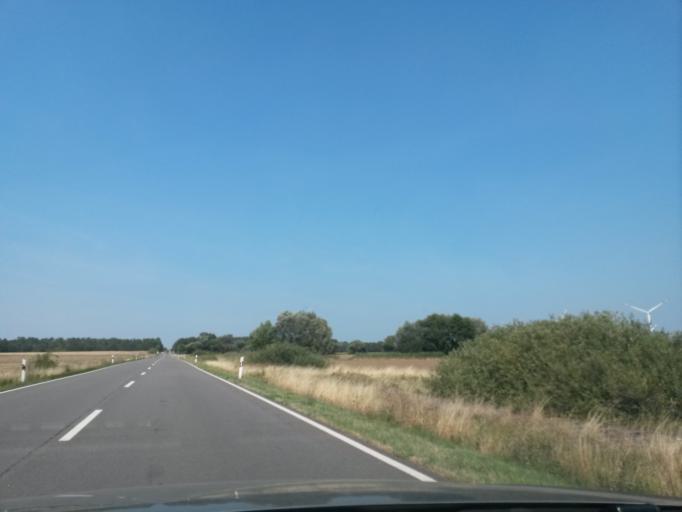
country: DE
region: Saxony-Anhalt
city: Jerichow
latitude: 52.5199
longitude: 12.0158
